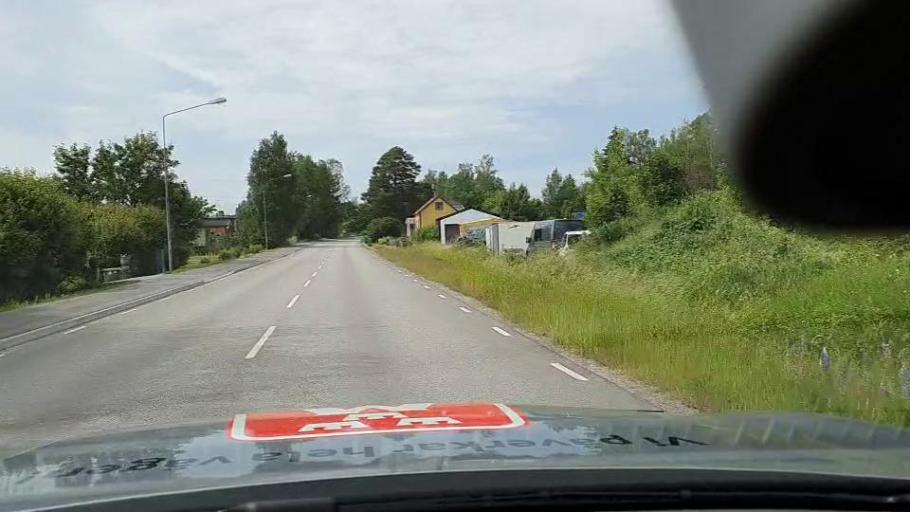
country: SE
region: Soedermanland
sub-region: Eskilstuna Kommun
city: Arla
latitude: 59.2796
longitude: 16.6823
